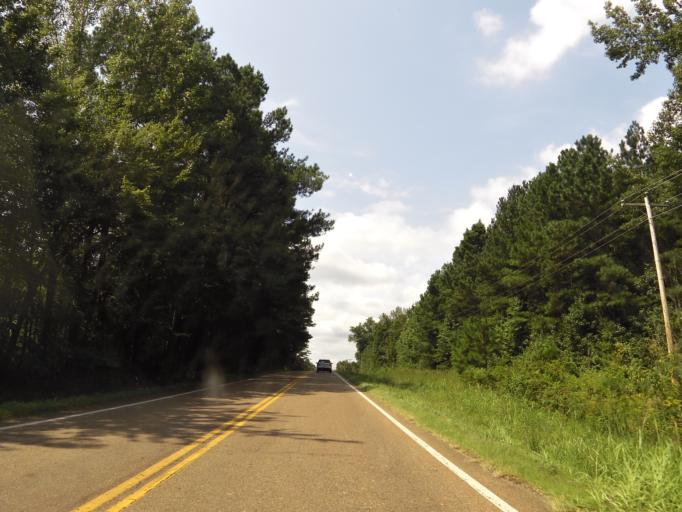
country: US
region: Tennessee
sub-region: Decatur County
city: Decaturville
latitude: 35.5463
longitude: -88.1883
